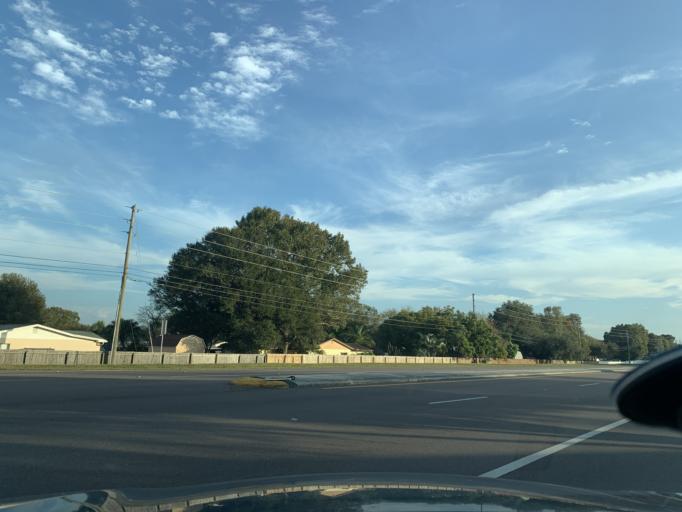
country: US
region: Florida
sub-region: Pinellas County
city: Ridgecrest
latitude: 27.8838
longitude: -82.7954
